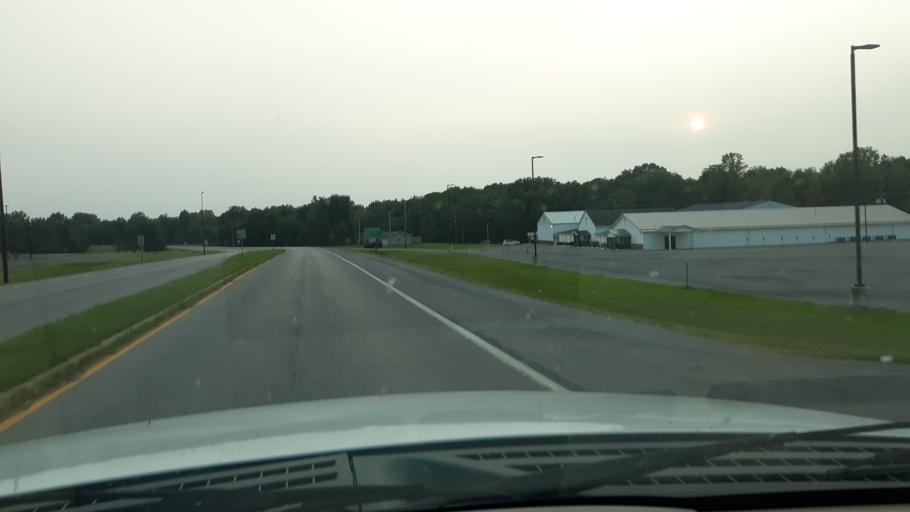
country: US
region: Illinois
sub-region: White County
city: Norris City
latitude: 37.9656
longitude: -88.3293
